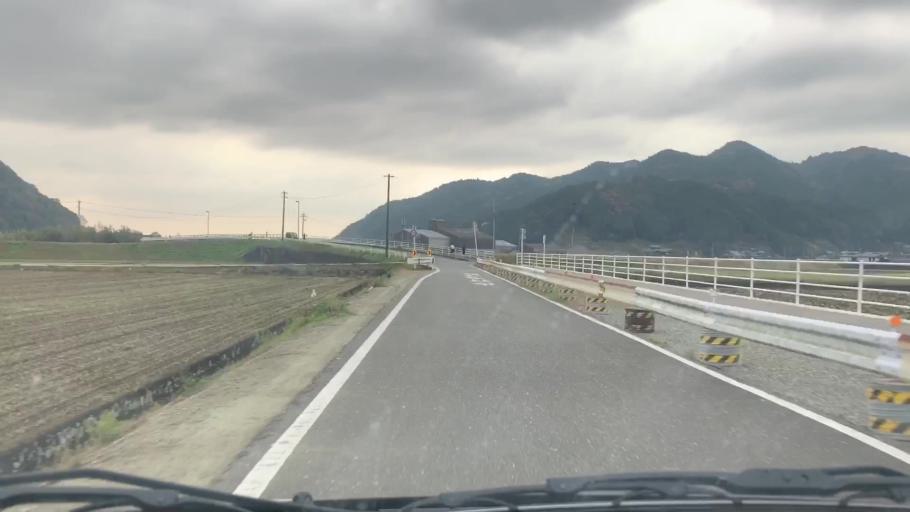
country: JP
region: Saga Prefecture
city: Ureshinomachi-shimojuku
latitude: 33.1264
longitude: 130.0342
